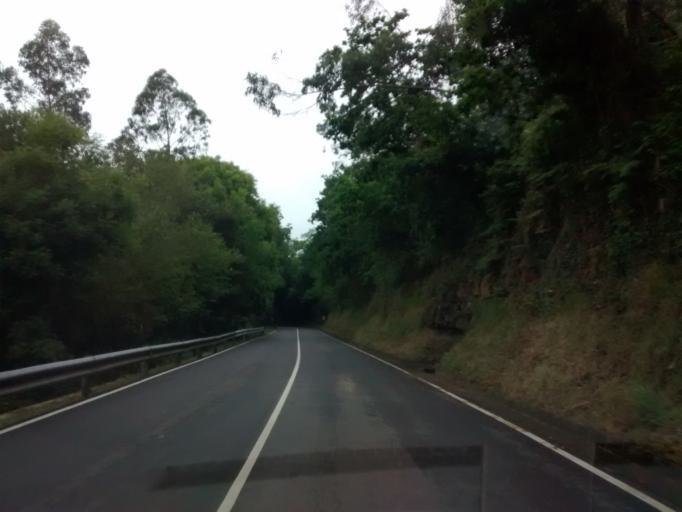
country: ES
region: Asturias
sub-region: Province of Asturias
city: Villaviciosa
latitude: 43.5370
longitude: -5.4130
